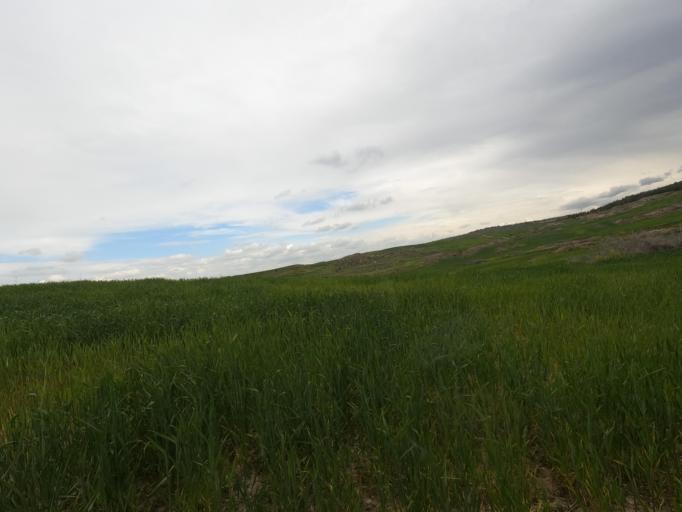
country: CY
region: Lefkosia
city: Astromeritis
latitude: 35.0991
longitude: 32.9486
